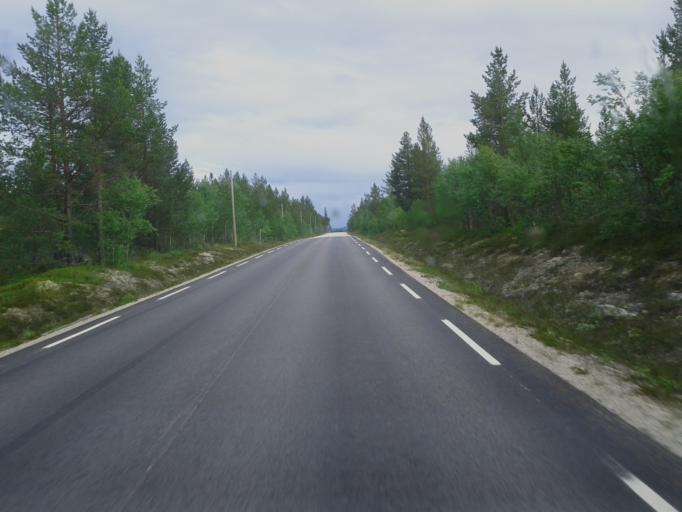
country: NO
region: Hedmark
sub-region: Engerdal
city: Engerdal
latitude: 62.0464
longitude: 11.6922
